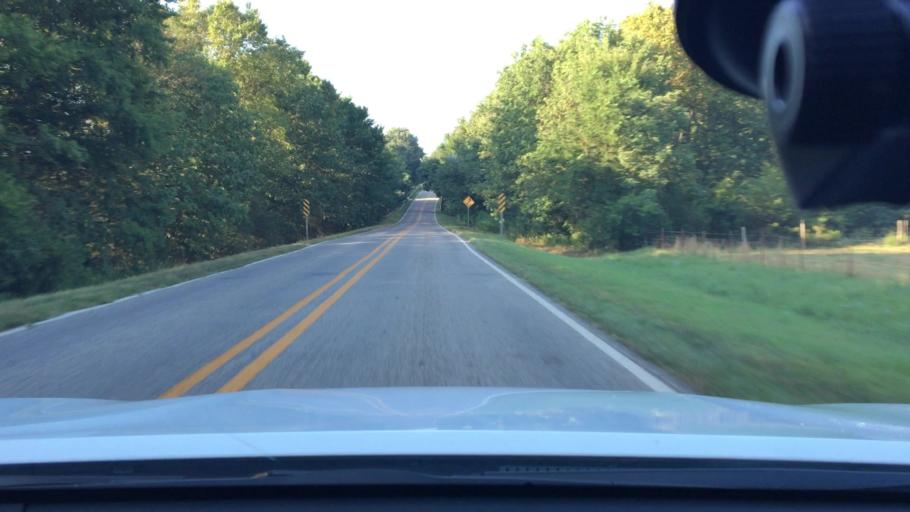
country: US
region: Arkansas
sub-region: Logan County
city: Paris
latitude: 35.3162
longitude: -93.6324
